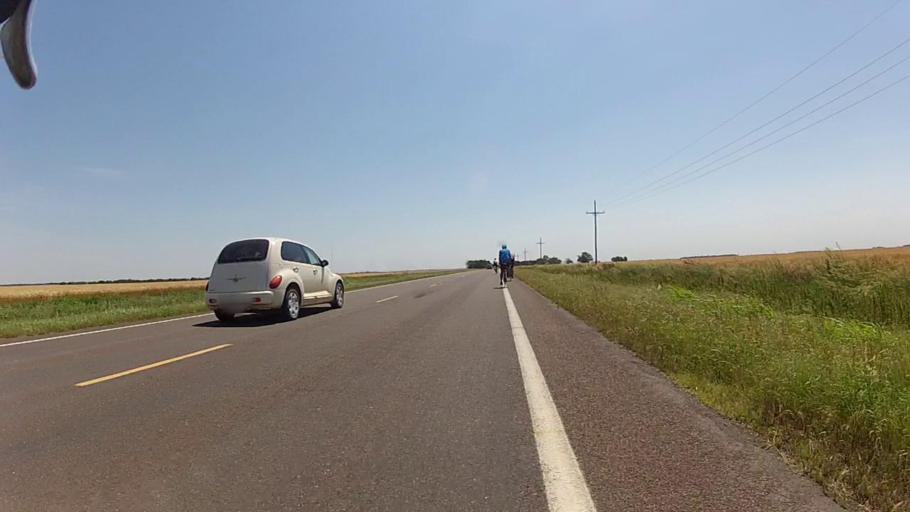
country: US
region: Kansas
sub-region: Sumner County
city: Caldwell
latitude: 37.0332
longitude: -97.5523
